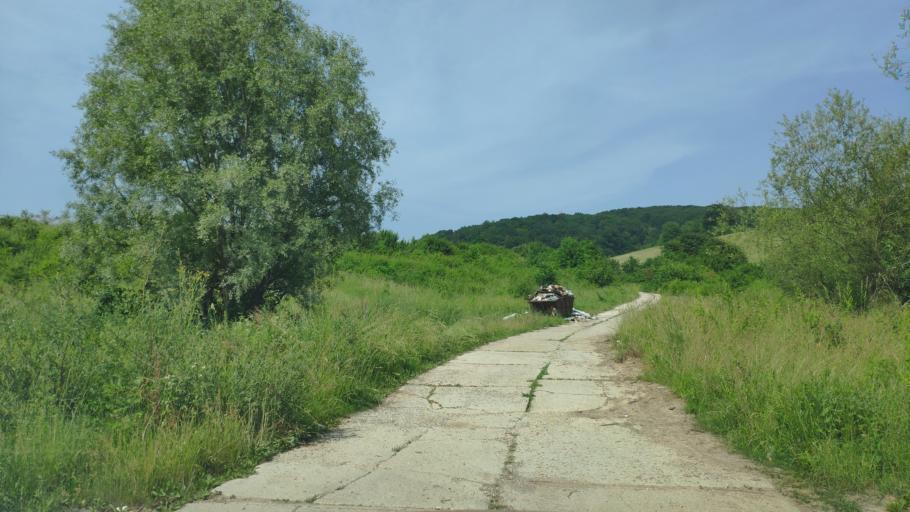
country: SK
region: Presovsky
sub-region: Okres Presov
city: Presov
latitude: 48.9636
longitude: 21.1421
